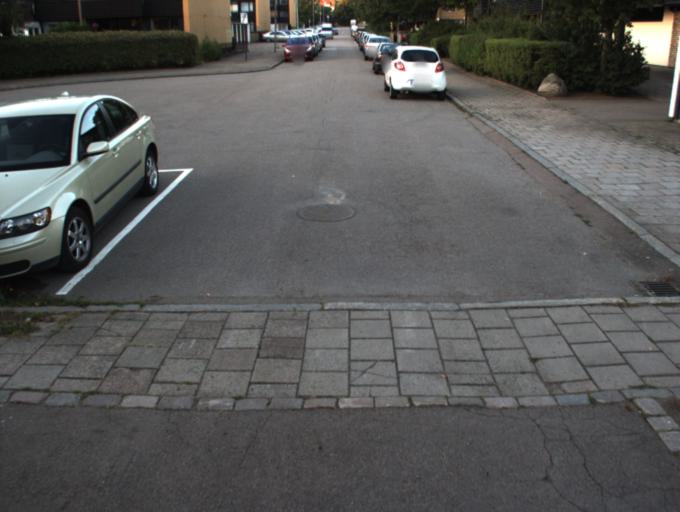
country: SE
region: Skane
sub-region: Helsingborg
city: Helsingborg
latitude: 56.0269
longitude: 12.7288
